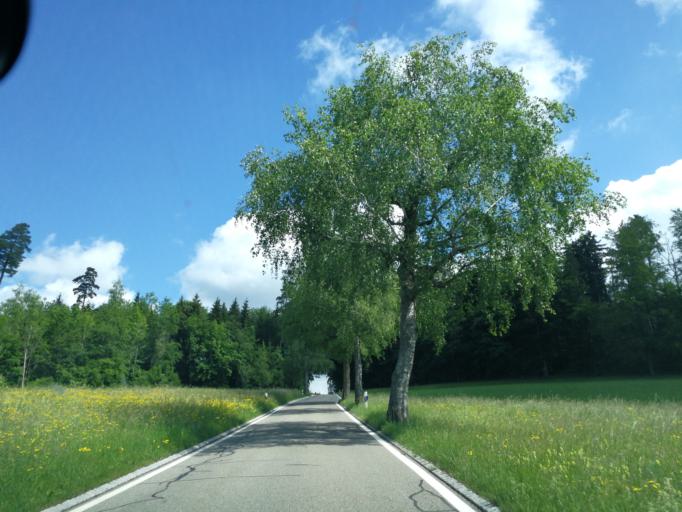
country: CH
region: Zurich
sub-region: Bezirk Meilen
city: Erlenbach / rechts des Dorfbachs oberhalb Bahnlinie
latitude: 47.3089
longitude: 8.6194
